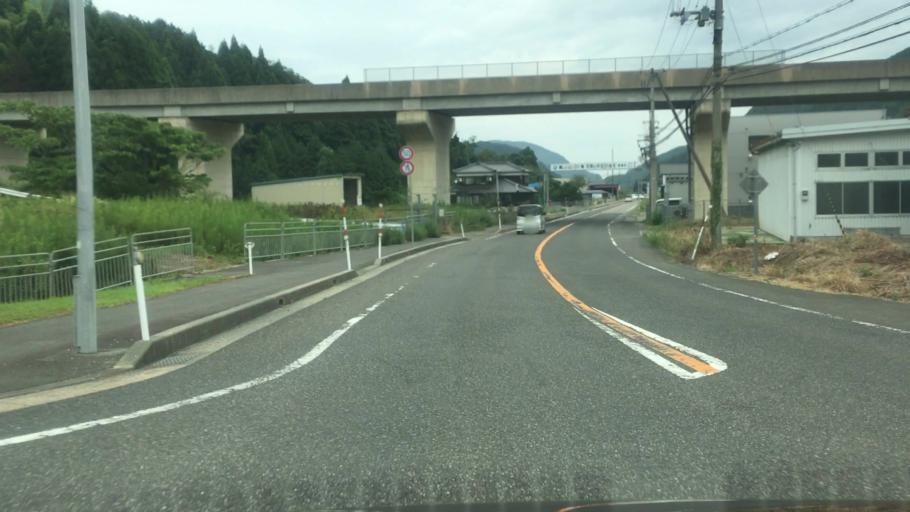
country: JP
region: Hyogo
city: Toyooka
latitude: 35.6282
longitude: 134.6785
